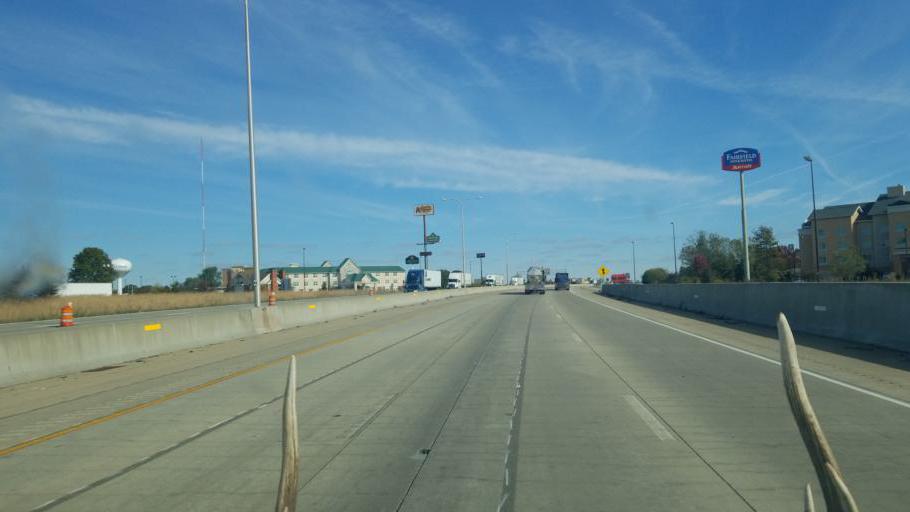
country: US
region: Illinois
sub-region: Effingham County
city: Effingham
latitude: 39.1358
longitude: -88.5614
